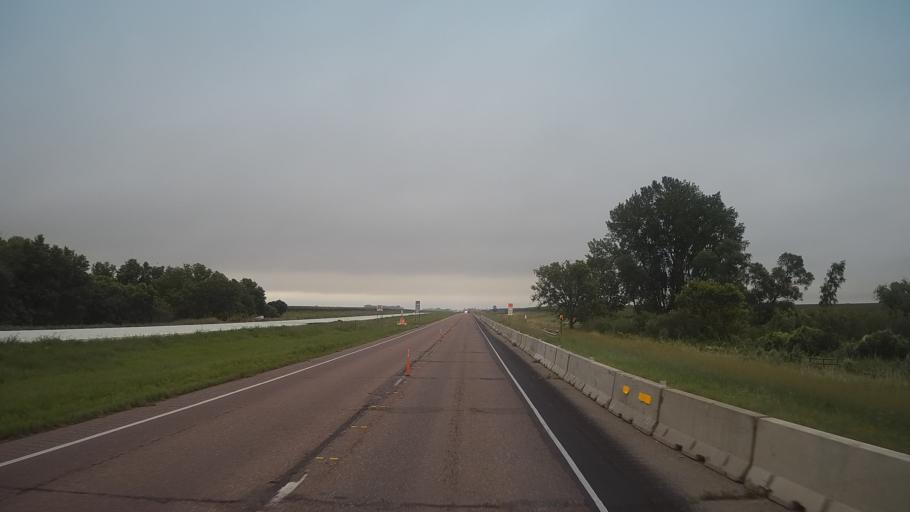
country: US
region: Minnesota
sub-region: Faribault County
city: Winnebago
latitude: 43.6662
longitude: -94.2791
